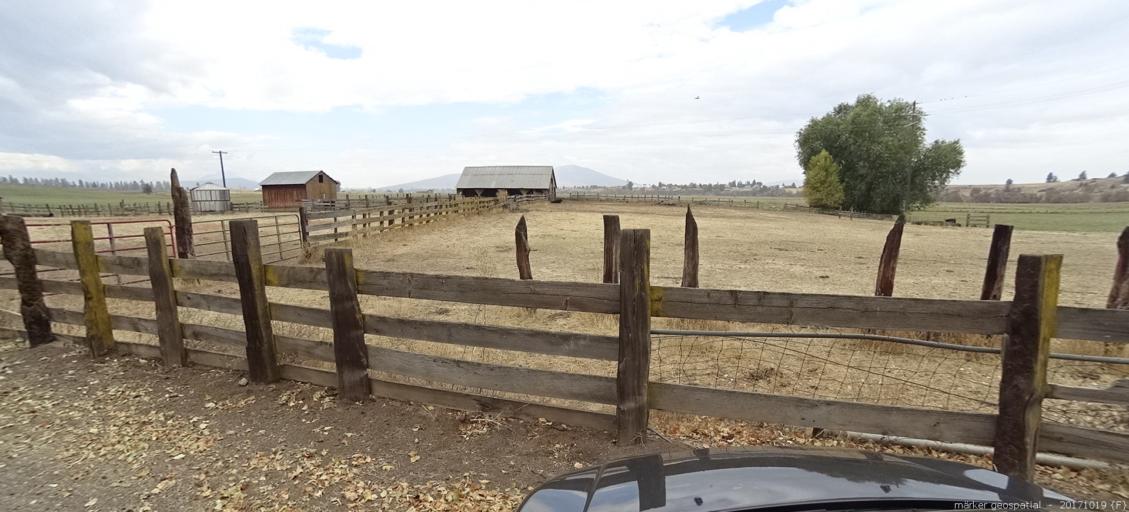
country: US
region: California
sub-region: Shasta County
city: Burney
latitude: 41.0495
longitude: -121.3752
